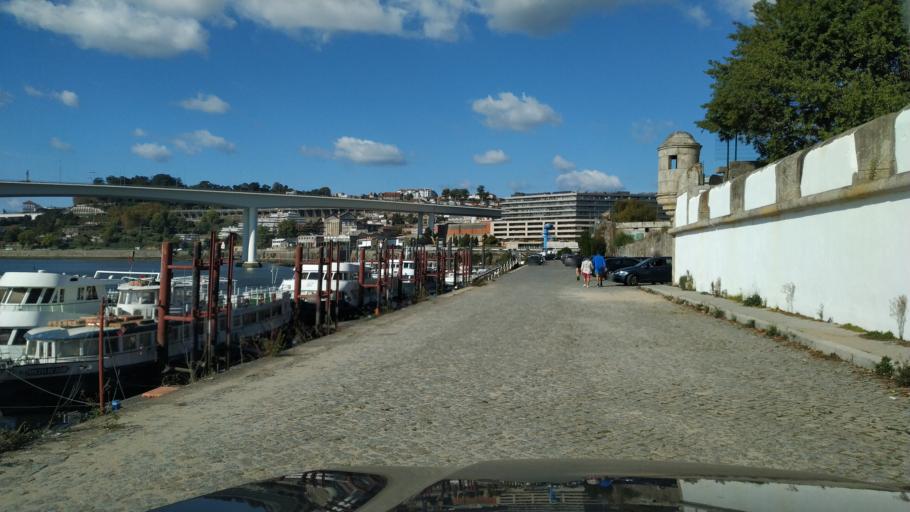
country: PT
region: Porto
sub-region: Gondomar
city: Valbom
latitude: 41.1423
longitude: -8.5755
